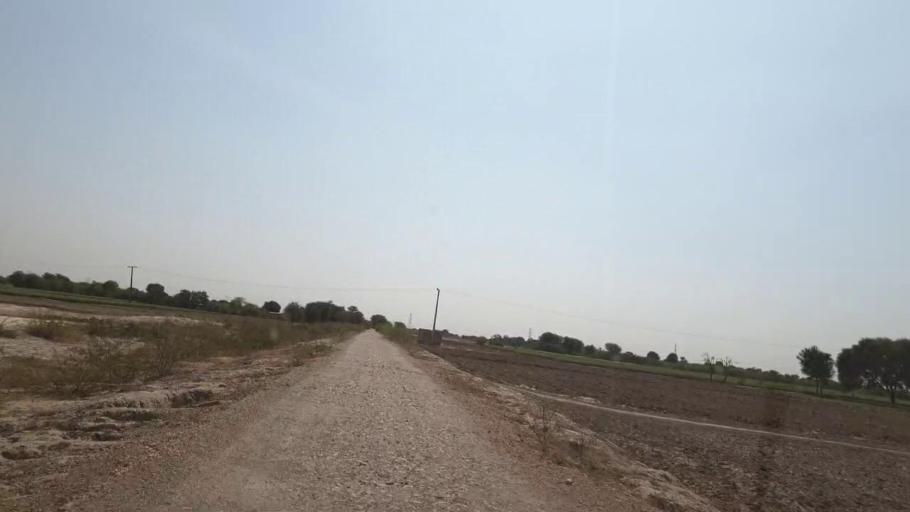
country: PK
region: Sindh
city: Nabisar
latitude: 25.0696
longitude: 69.5527
